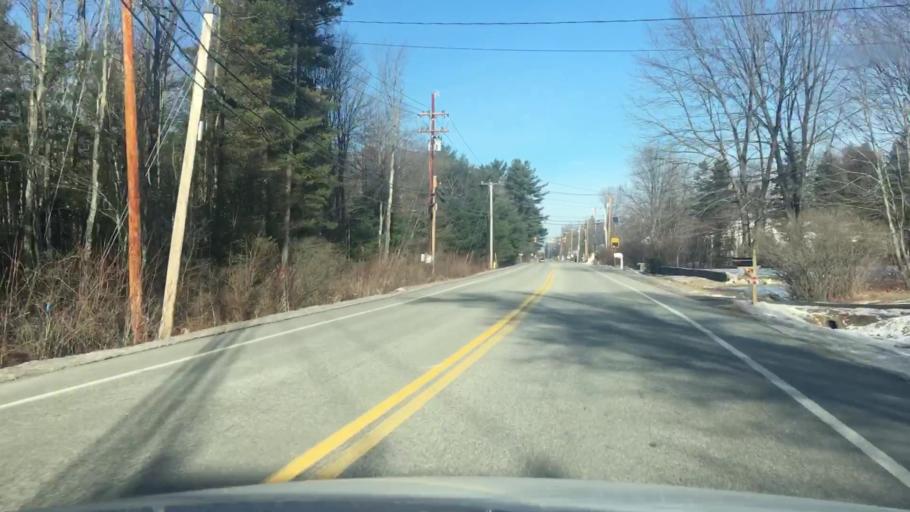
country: US
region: Maine
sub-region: Androscoggin County
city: Auburn
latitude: 44.0857
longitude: -70.2621
